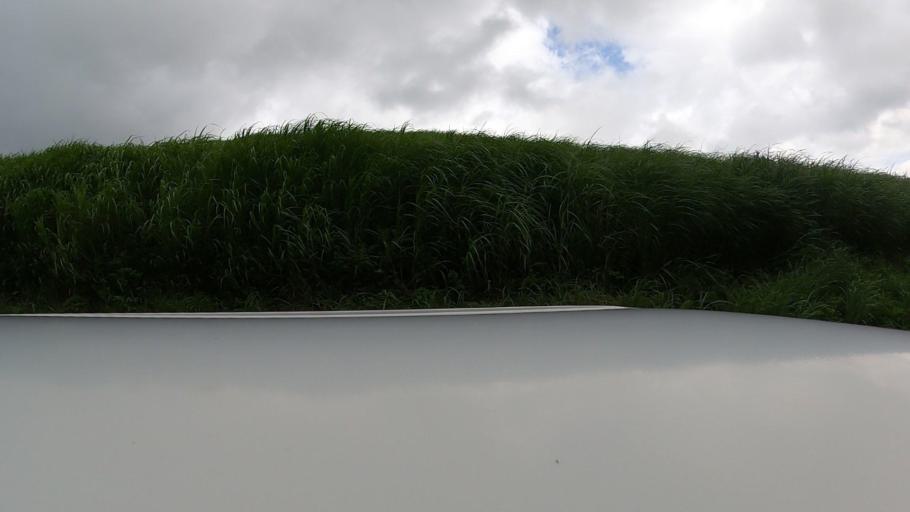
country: JP
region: Kumamoto
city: Aso
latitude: 32.9533
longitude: 131.1661
